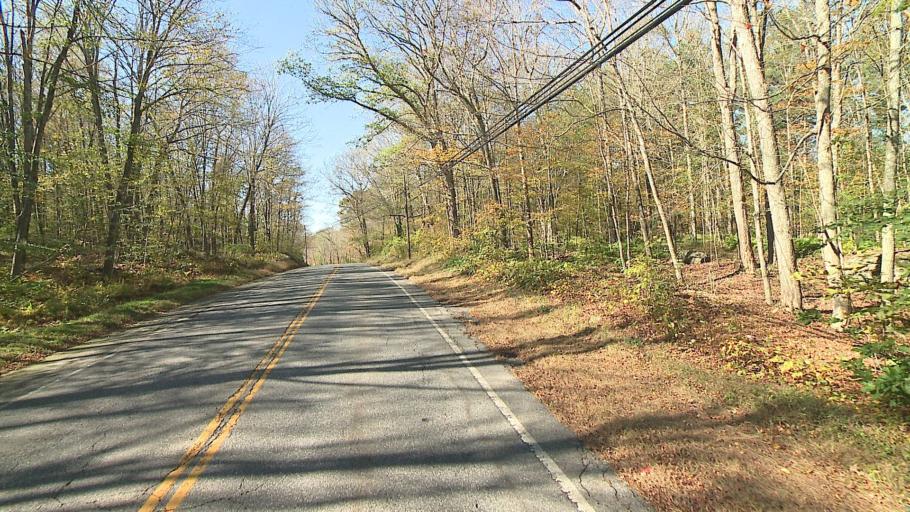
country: US
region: Connecticut
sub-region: Hartford County
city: Terramuggus
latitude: 41.6481
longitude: -72.4263
